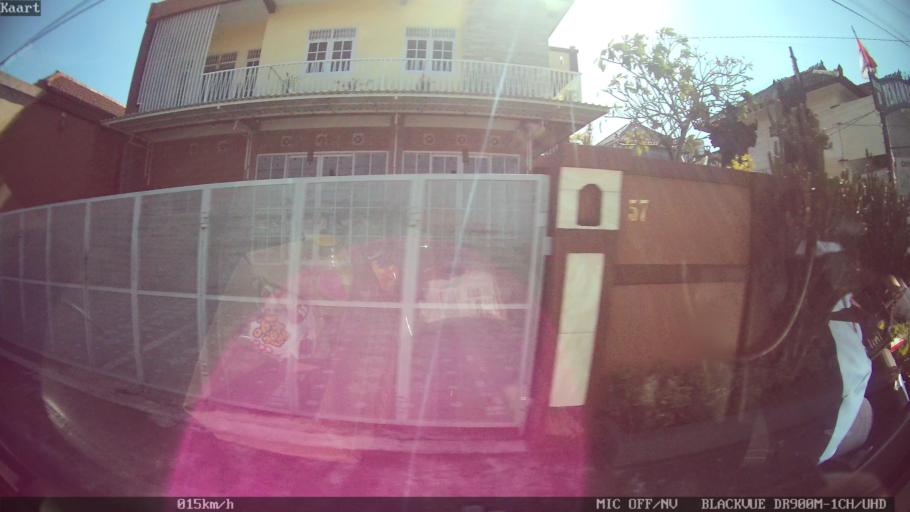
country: ID
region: Bali
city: Banjar Kertasari
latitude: -8.6418
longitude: 115.1914
